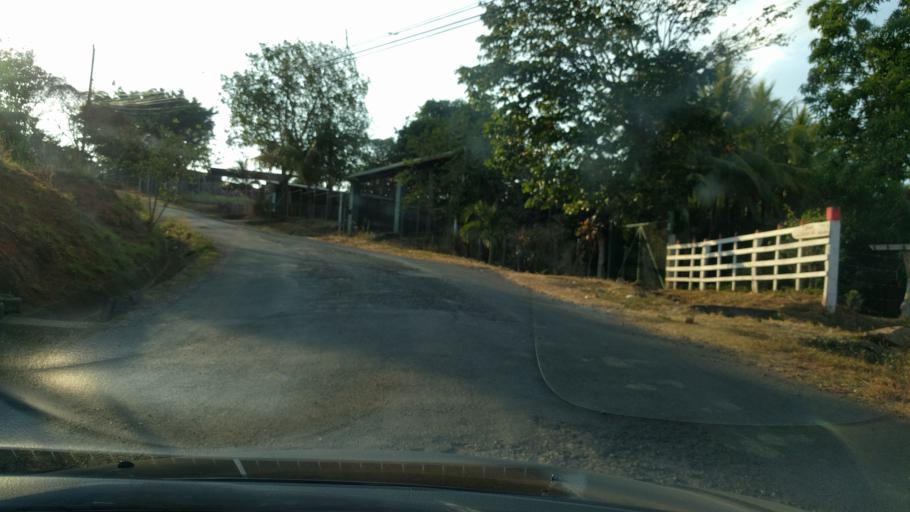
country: CR
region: Puntarenas
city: Esparza
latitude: 10.0146
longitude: -84.6940
